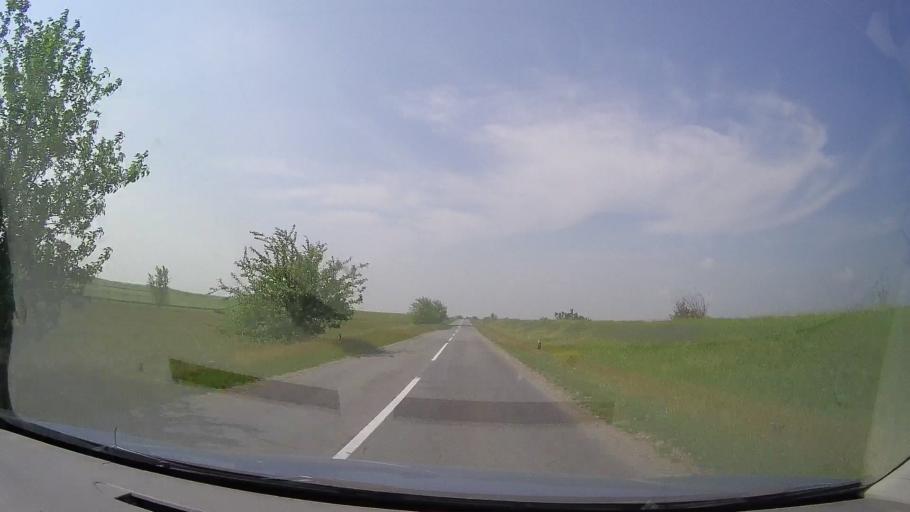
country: RS
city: Samos
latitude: 45.1773
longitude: 20.7590
